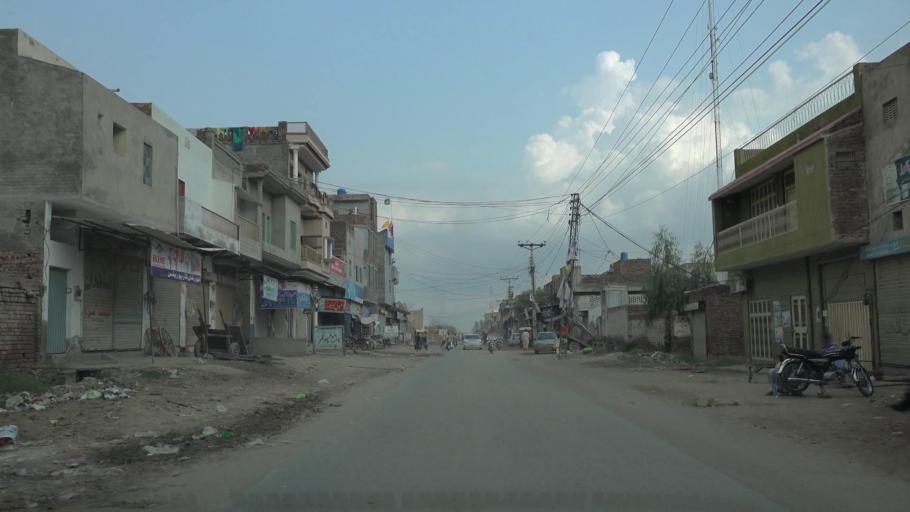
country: PK
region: Punjab
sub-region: Nankana Sahib District
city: Shahkot
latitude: 31.5688
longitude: 73.4894
